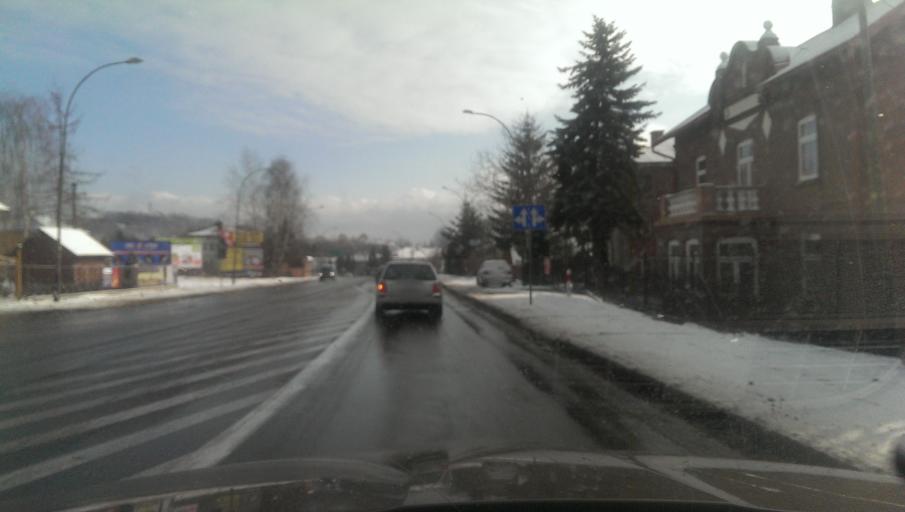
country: PL
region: Subcarpathian Voivodeship
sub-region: Powiat sanocki
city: Sanok
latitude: 49.5629
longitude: 22.1851
